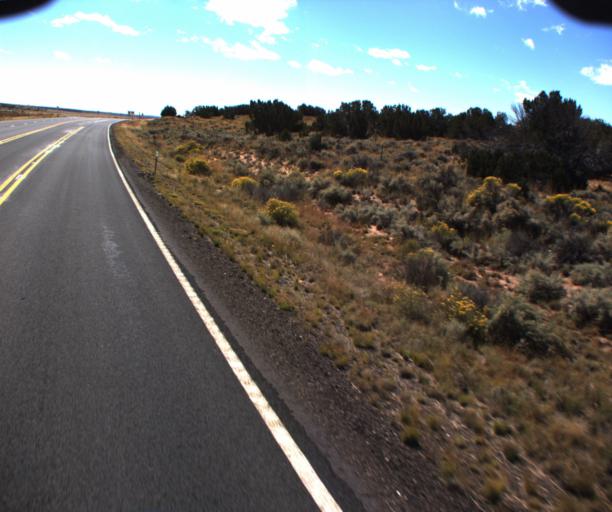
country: US
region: Arizona
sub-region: Apache County
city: Houck
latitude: 35.0022
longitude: -109.2277
